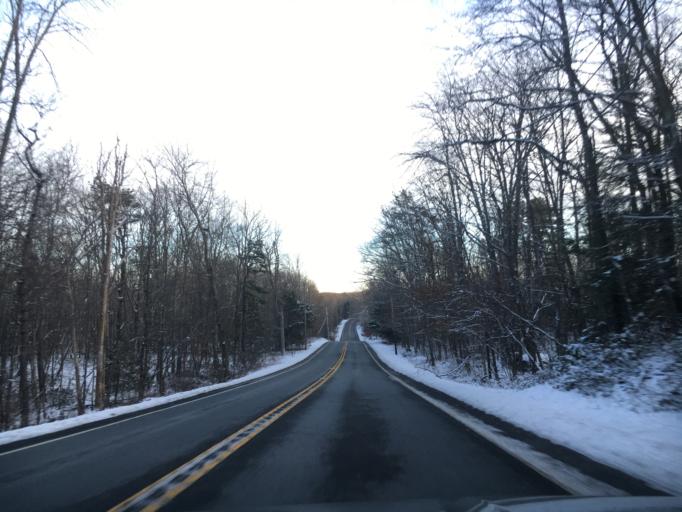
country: US
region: Pennsylvania
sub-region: Pike County
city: Hemlock Farms
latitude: 41.2958
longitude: -75.0948
